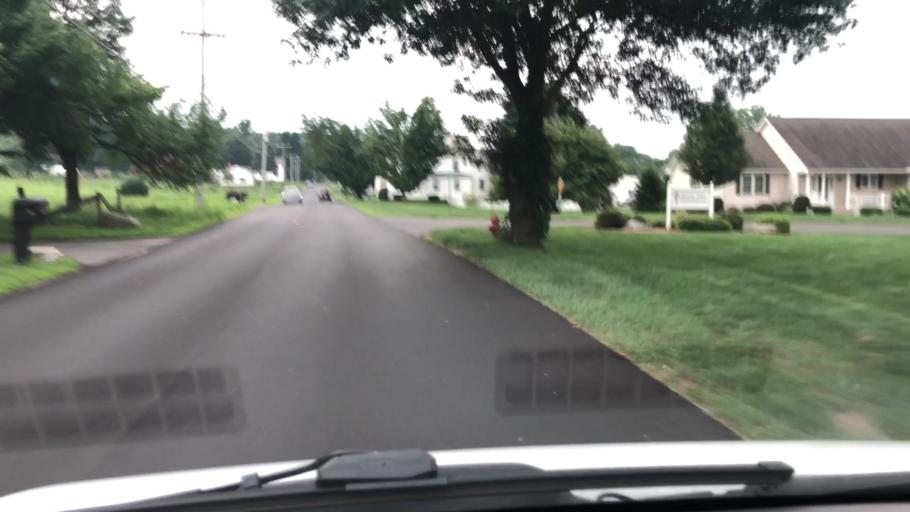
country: US
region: Massachusetts
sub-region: Hampshire County
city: Easthampton
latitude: 42.2730
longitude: -72.6433
